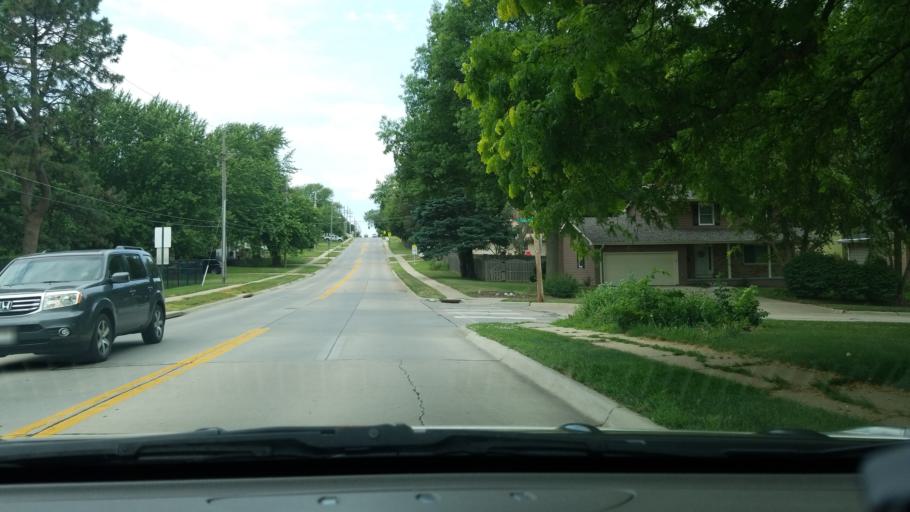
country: US
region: Nebraska
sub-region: Sarpy County
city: Papillion
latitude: 41.1436
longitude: -96.0338
